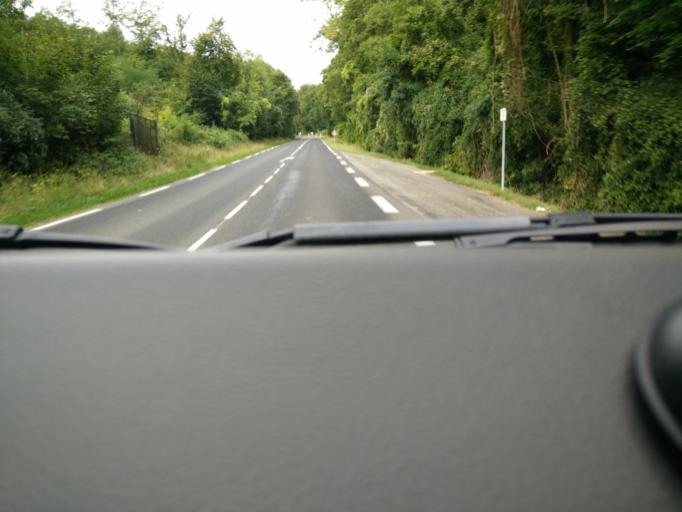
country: FR
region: Lorraine
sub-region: Departement de Meurthe-et-Moselle
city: Montauville
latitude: 48.9001
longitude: 5.9986
